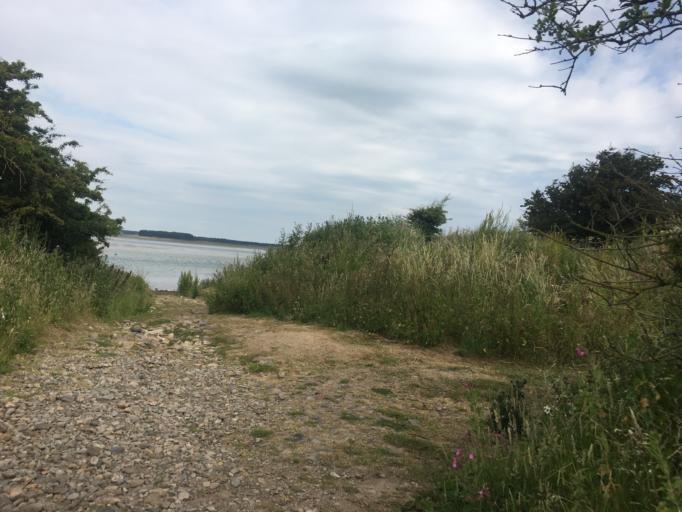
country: GB
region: England
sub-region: Northumberland
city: Bamburgh
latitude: 55.6111
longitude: -1.7578
